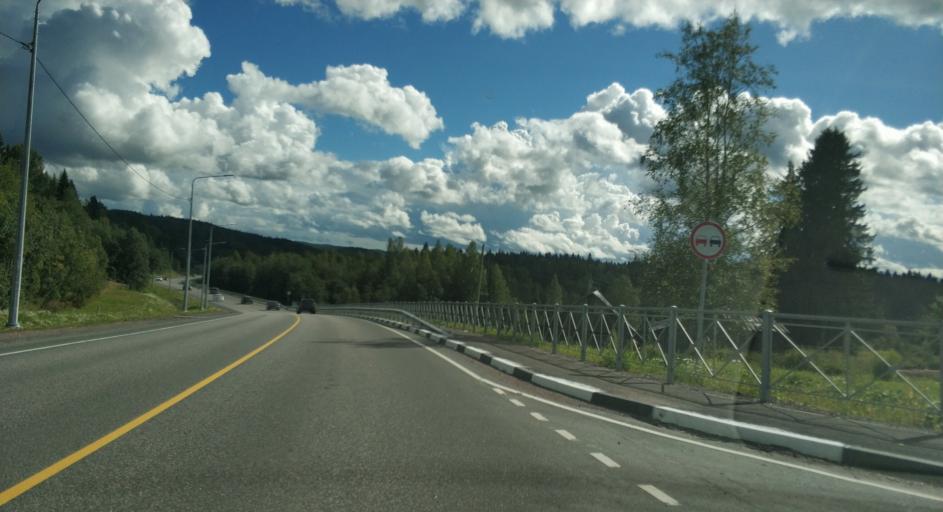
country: RU
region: Republic of Karelia
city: Ruskeala
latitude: 61.9229
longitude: 30.6074
